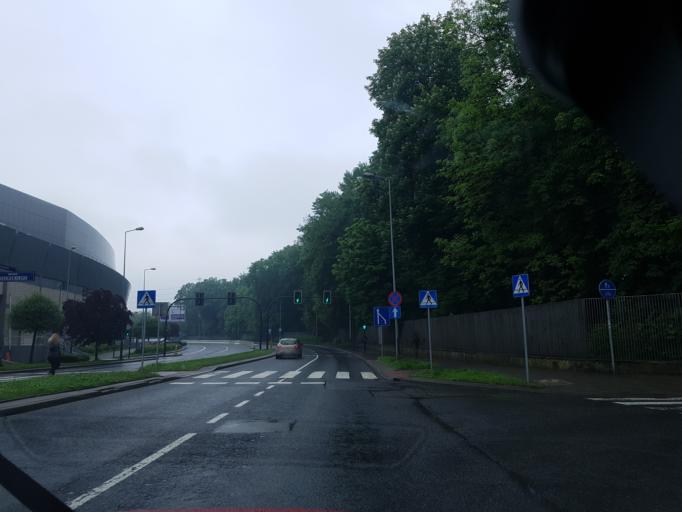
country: PL
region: Lesser Poland Voivodeship
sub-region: Krakow
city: Krakow
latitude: 50.0543
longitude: 19.9537
